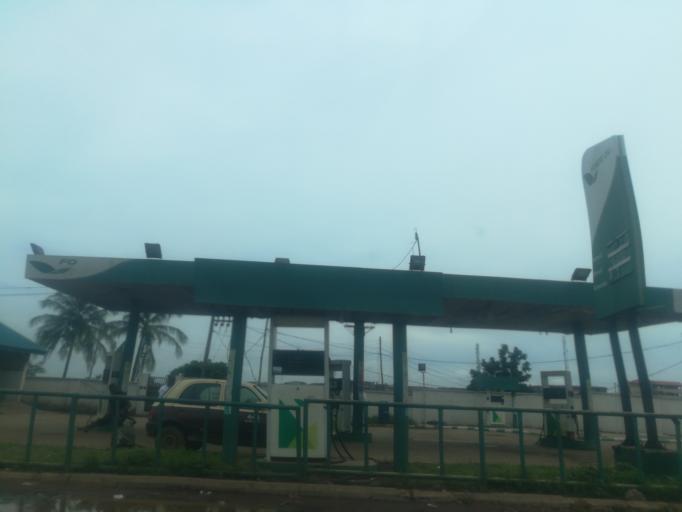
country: NG
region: Oyo
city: Ibadan
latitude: 7.3659
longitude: 3.9271
